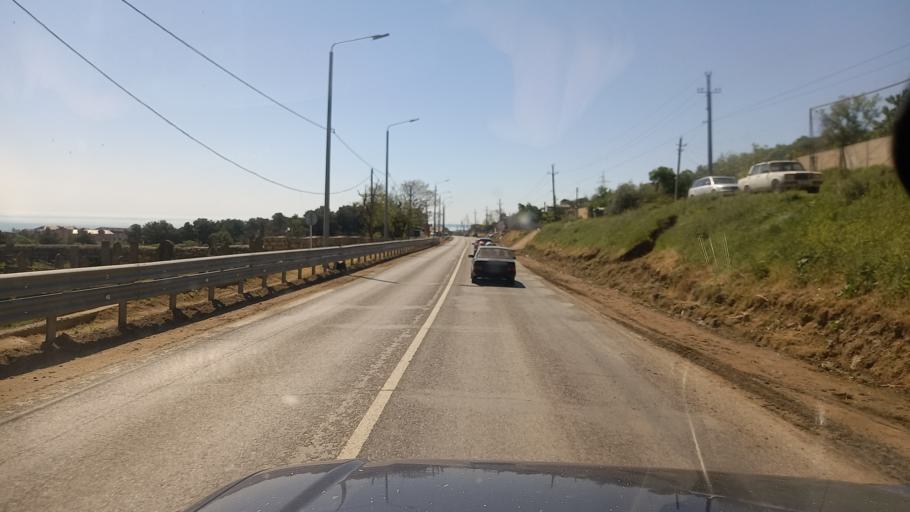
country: RU
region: Dagestan
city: Derbent
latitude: 42.0486
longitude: 48.2830
